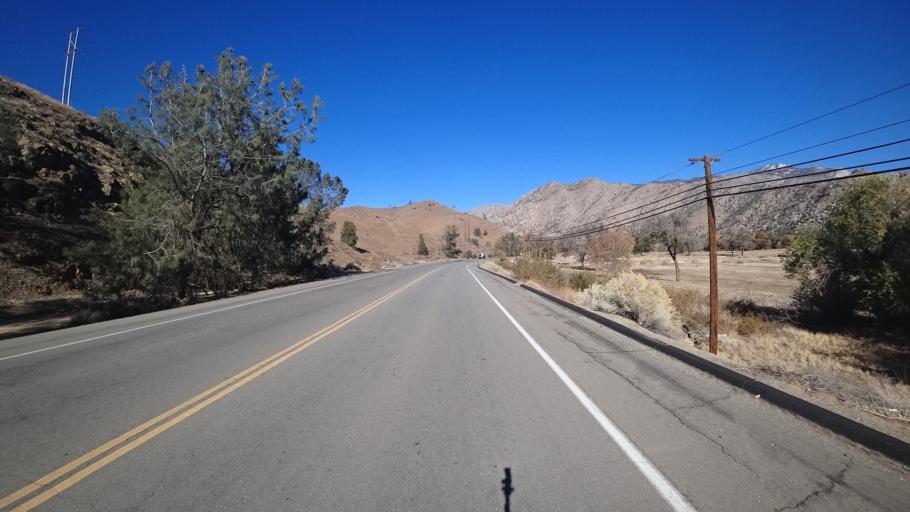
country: US
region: California
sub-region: Kern County
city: Kernville
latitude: 35.7382
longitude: -118.4269
